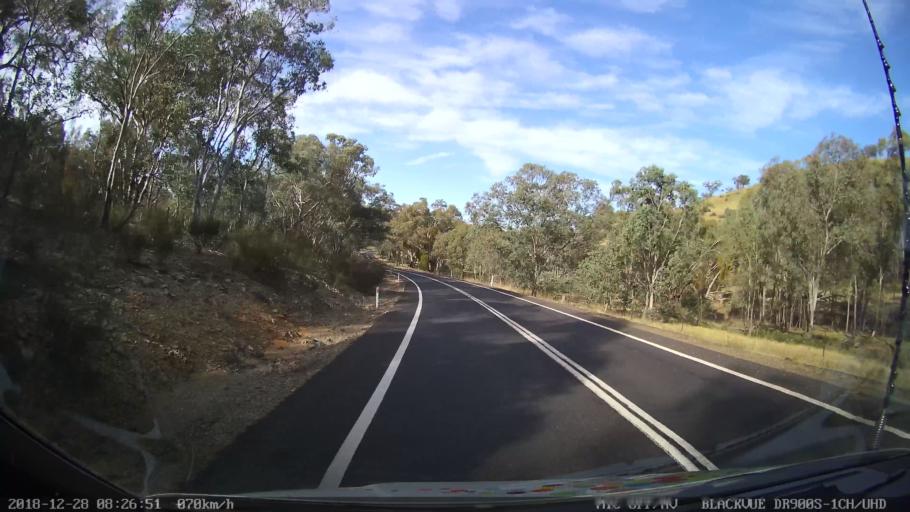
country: AU
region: New South Wales
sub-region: Blayney
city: Blayney
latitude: -33.9388
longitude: 149.3430
